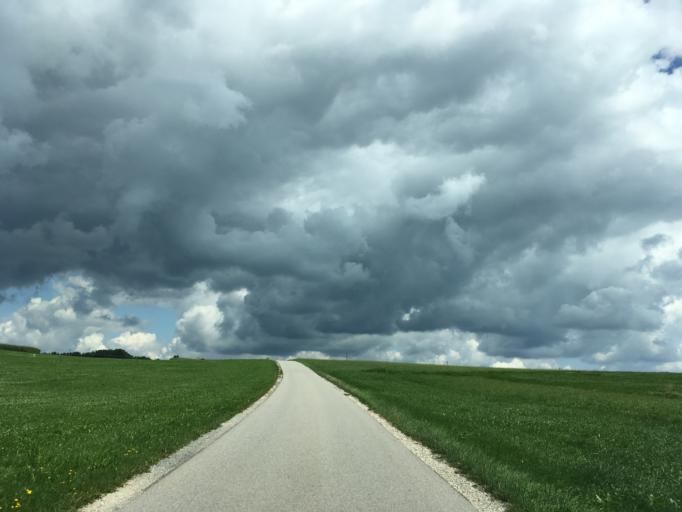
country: DE
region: Bavaria
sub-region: Upper Bavaria
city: Amerang
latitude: 47.9907
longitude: 12.3409
